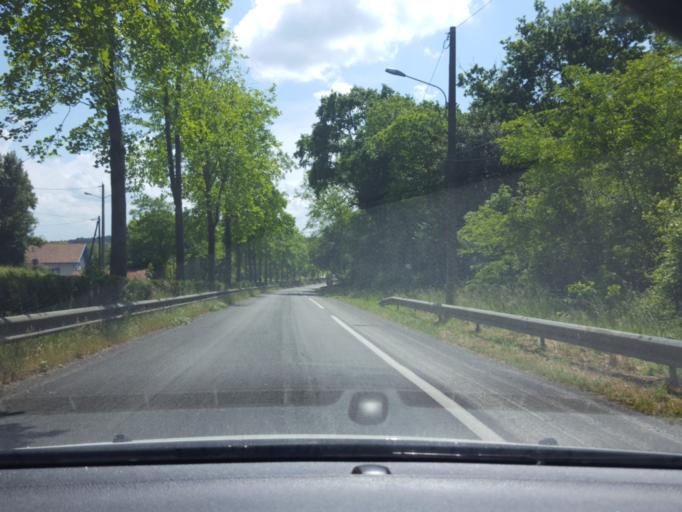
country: FR
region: Aquitaine
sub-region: Departement des Landes
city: Ondres
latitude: 43.5574
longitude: -1.4536
